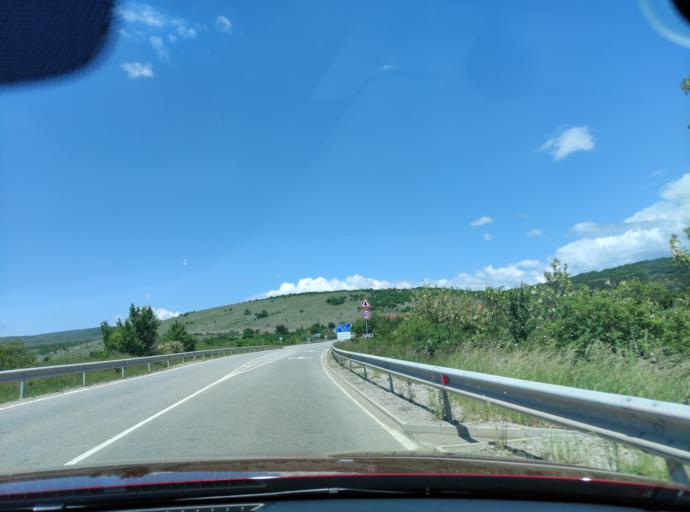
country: BG
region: Sofiya
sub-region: Obshtina Kostinbrod
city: Kostinbrod
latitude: 42.8831
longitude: 23.1649
